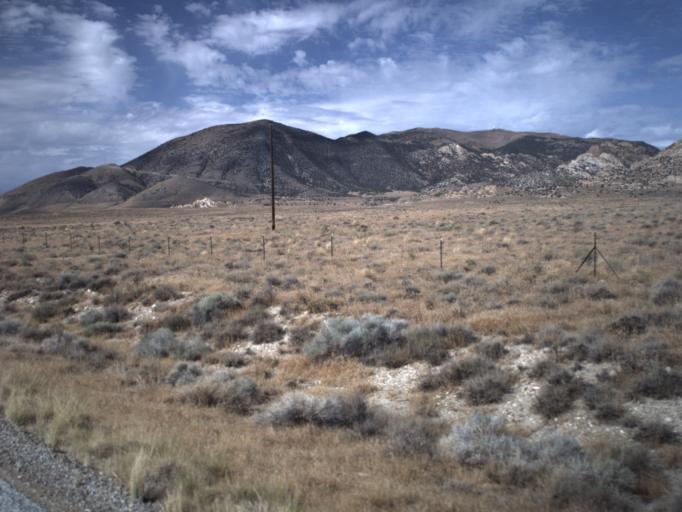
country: US
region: Utah
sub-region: Tooele County
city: Wendover
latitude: 41.4979
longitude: -113.6108
